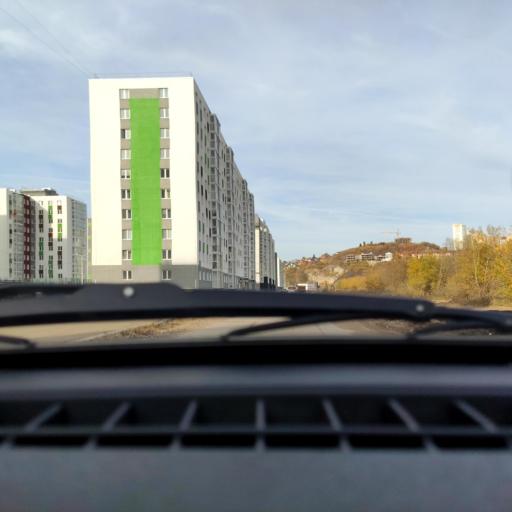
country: RU
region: Bashkortostan
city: Ufa
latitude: 54.6898
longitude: 55.9727
